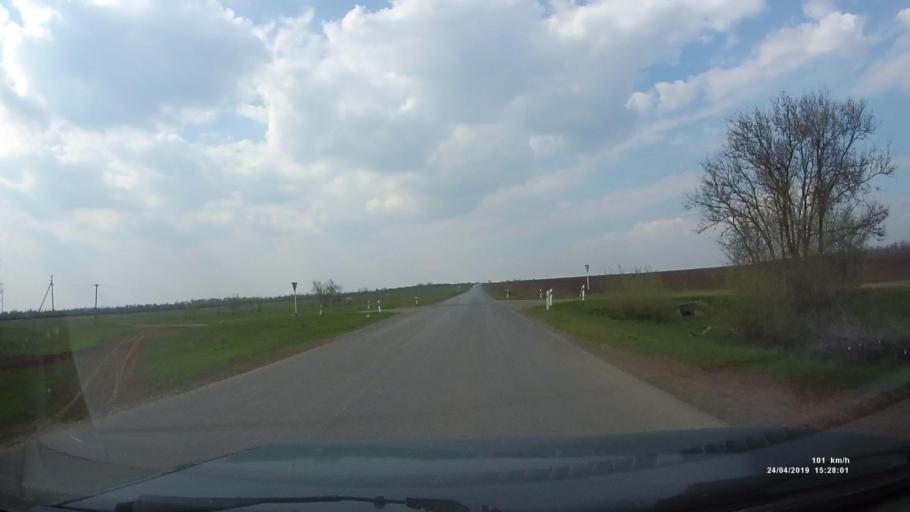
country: RU
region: Rostov
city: Remontnoye
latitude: 46.5729
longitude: 43.0215
